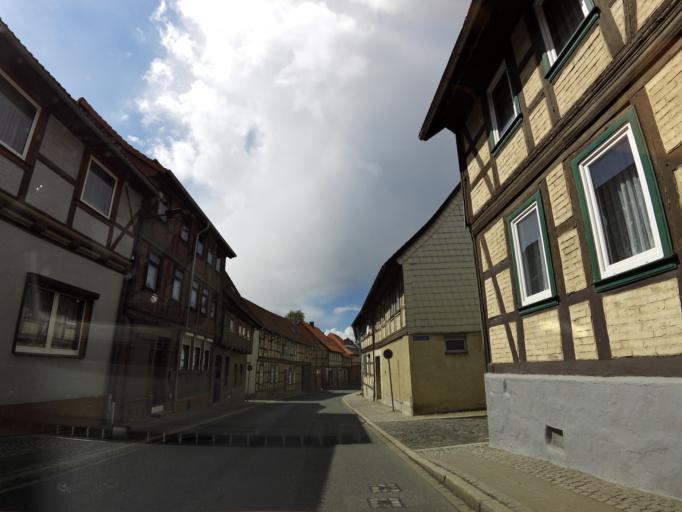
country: DE
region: Saxony-Anhalt
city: Derenburg
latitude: 51.8712
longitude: 10.9142
